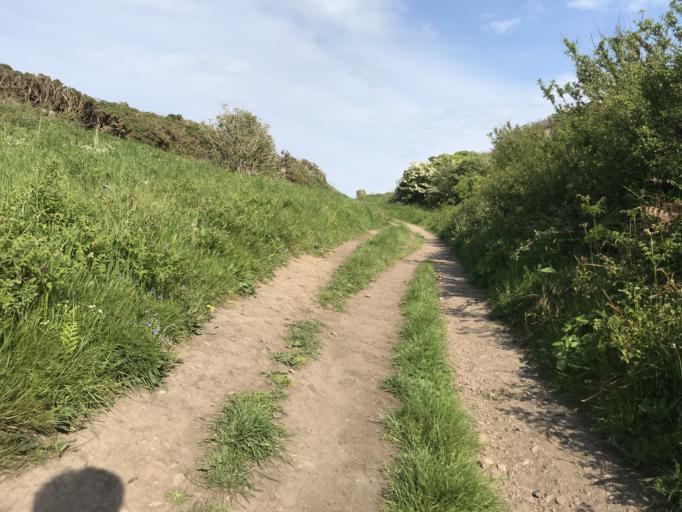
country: IE
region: Leinster
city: Sutton
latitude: 53.3684
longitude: -6.0904
